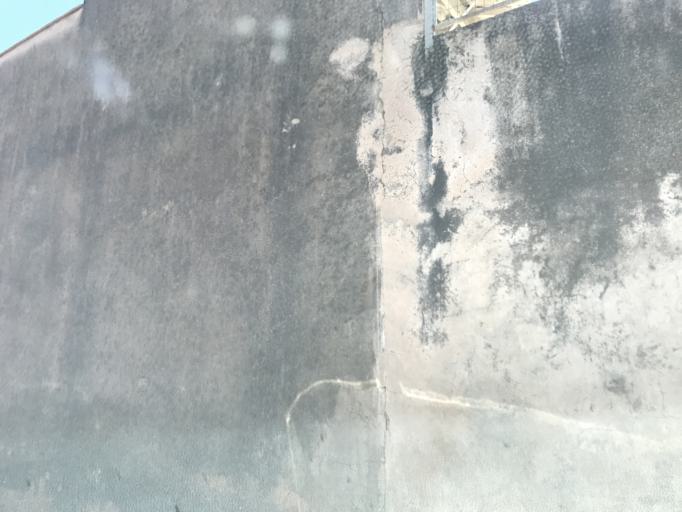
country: BR
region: Parana
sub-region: Londrina
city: Londrina
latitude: -23.3496
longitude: -51.1613
